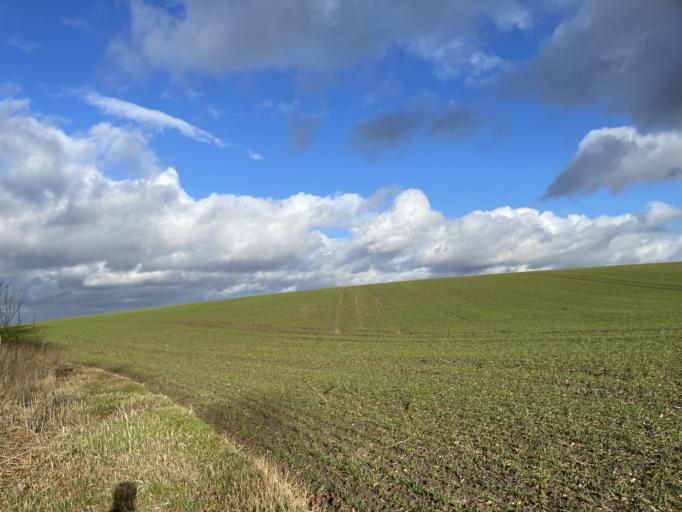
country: DK
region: Central Jutland
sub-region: Viborg Kommune
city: Bjerringbro
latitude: 56.2572
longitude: 9.6813
